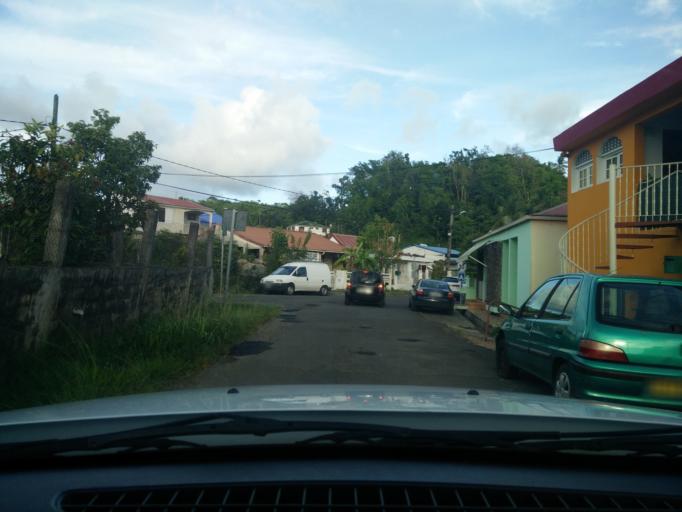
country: GP
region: Guadeloupe
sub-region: Guadeloupe
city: Les Abymes
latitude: 16.2517
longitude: -61.5104
